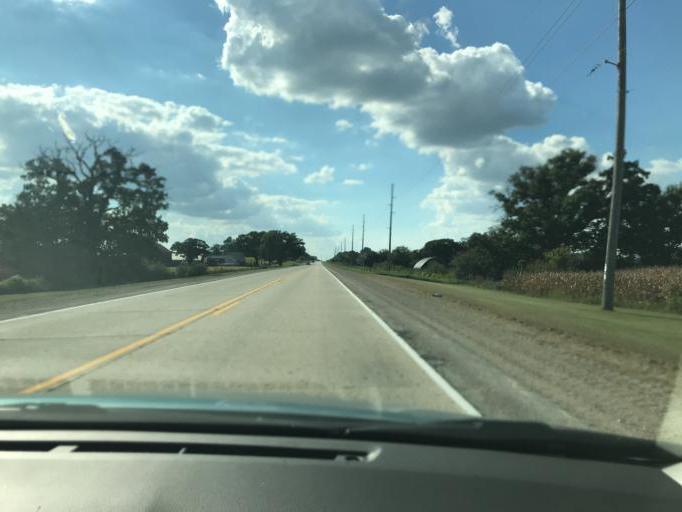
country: US
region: Wisconsin
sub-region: Rock County
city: Orfordville
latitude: 42.5572
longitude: -89.2911
